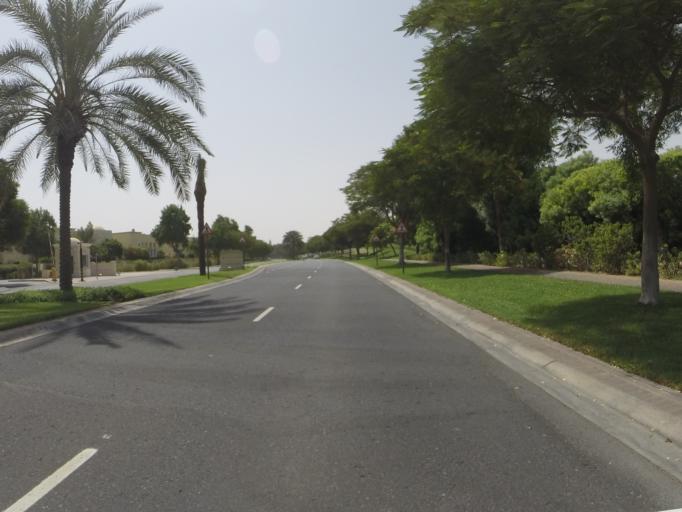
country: AE
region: Dubai
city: Dubai
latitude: 25.0570
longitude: 55.1640
